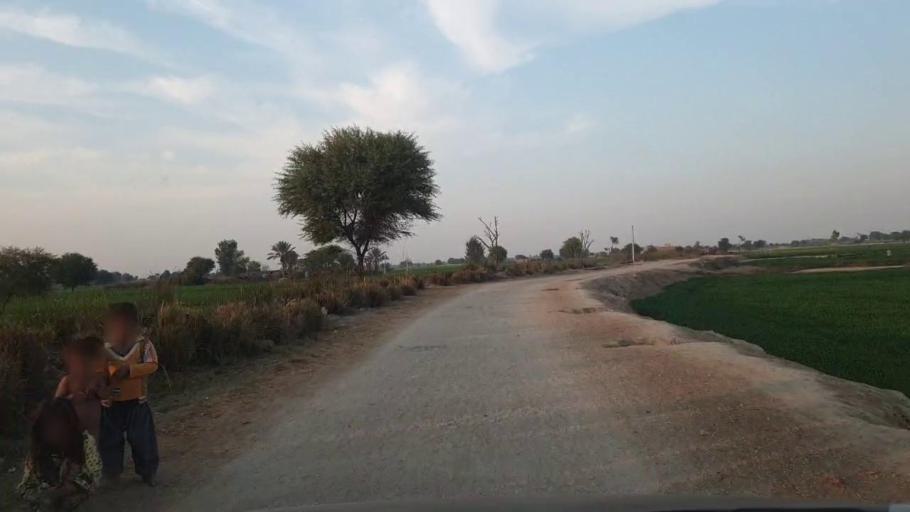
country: PK
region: Sindh
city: Shahpur Chakar
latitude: 26.1899
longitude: 68.6169
